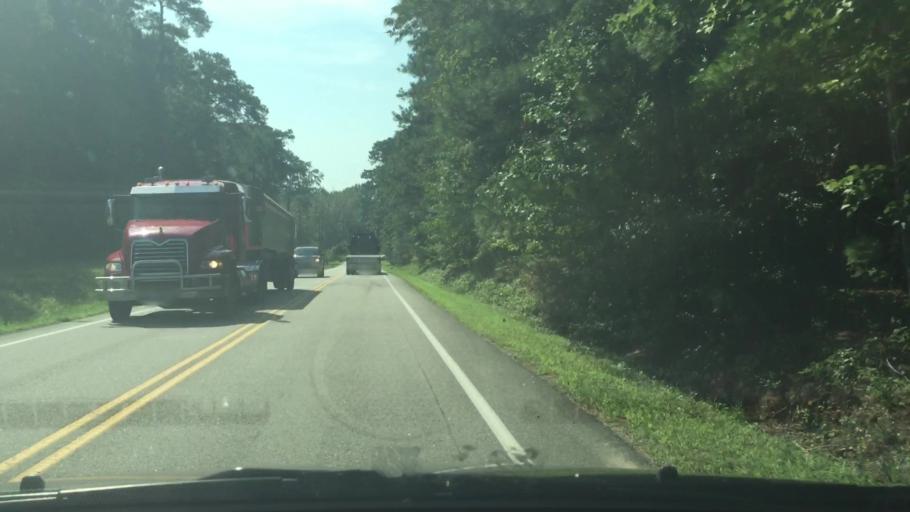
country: US
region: Virginia
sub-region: Sussex County
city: Sussex
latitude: 37.0496
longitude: -77.3169
